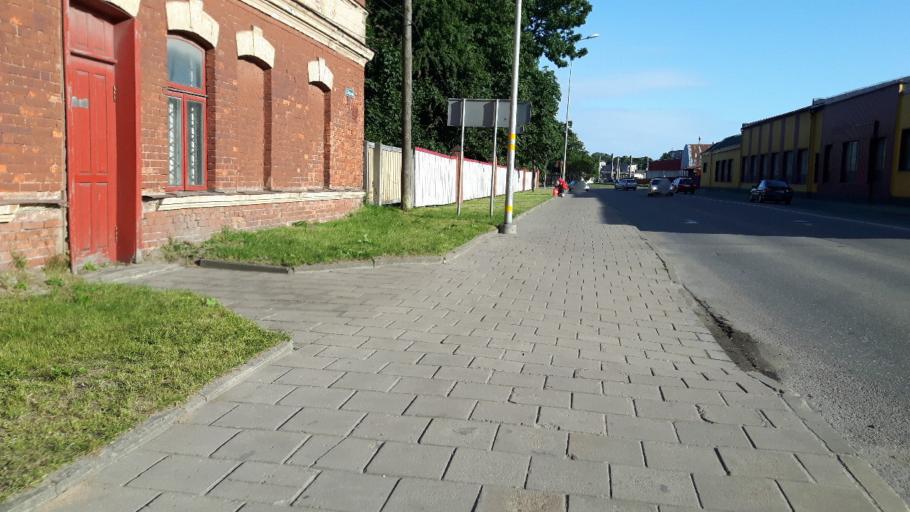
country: LV
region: Liepaja
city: Liepaja
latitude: 56.5229
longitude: 21.0046
